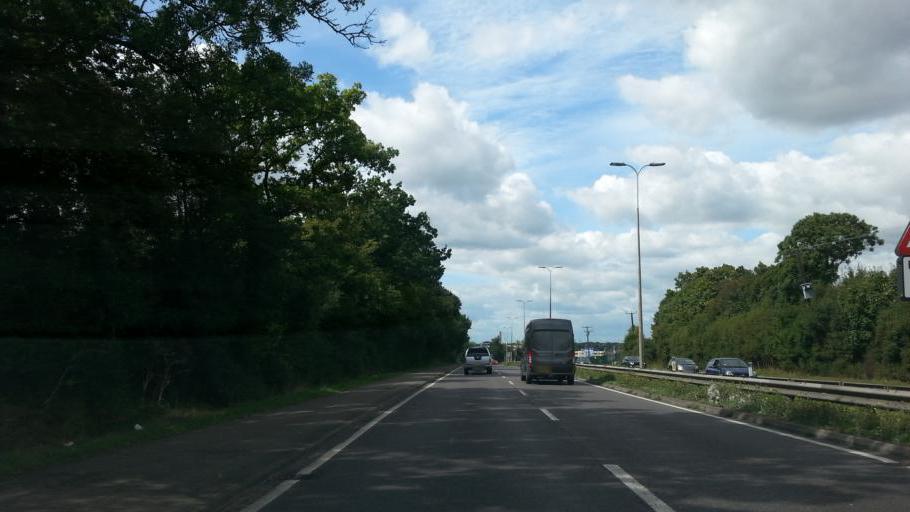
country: GB
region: England
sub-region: Essex
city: Wickford
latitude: 51.5901
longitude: 0.5242
